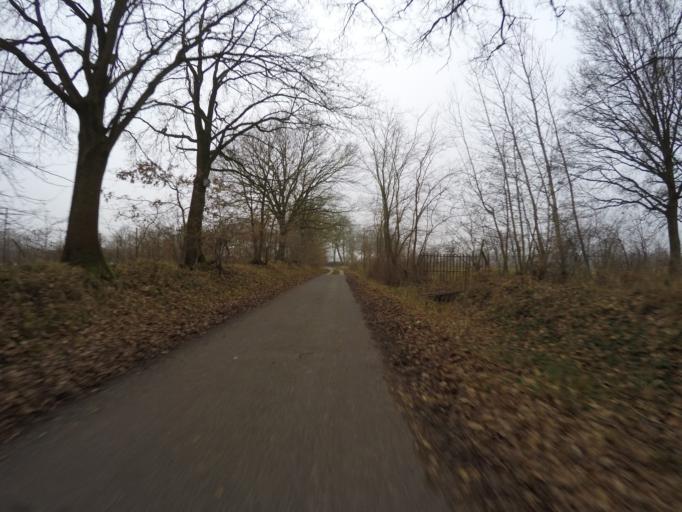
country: DE
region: Schleswig-Holstein
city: Tangstedt
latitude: 53.6716
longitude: 9.8317
